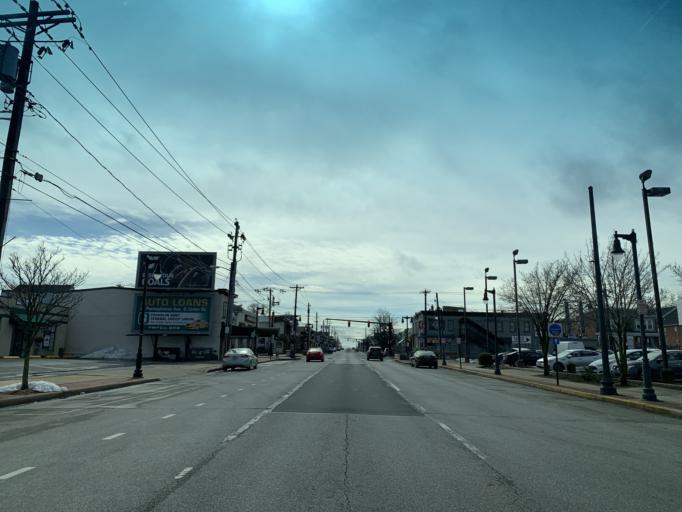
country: US
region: Delaware
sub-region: New Castle County
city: Wilmington
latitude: 39.7542
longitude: -75.5696
